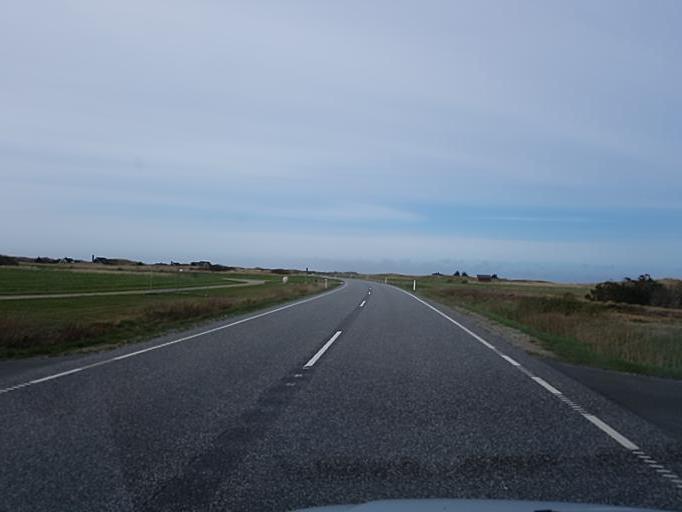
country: DK
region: Central Jutland
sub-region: Ringkobing-Skjern Kommune
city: Hvide Sande
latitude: 55.8846
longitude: 8.1761
